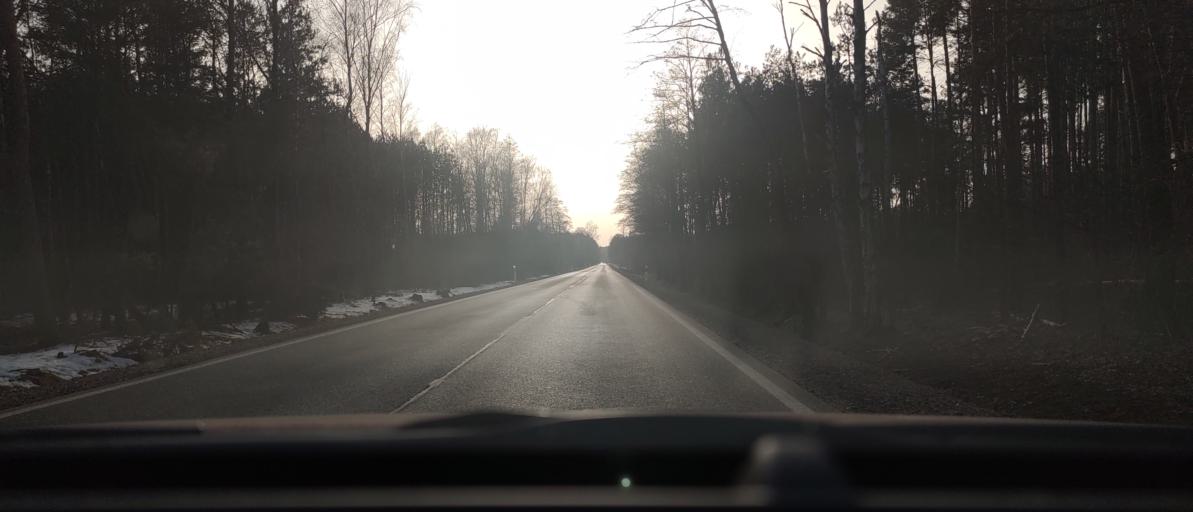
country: PL
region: Masovian Voivodeship
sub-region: Powiat bialobrzeski
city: Sucha
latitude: 51.6350
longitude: 20.9008
